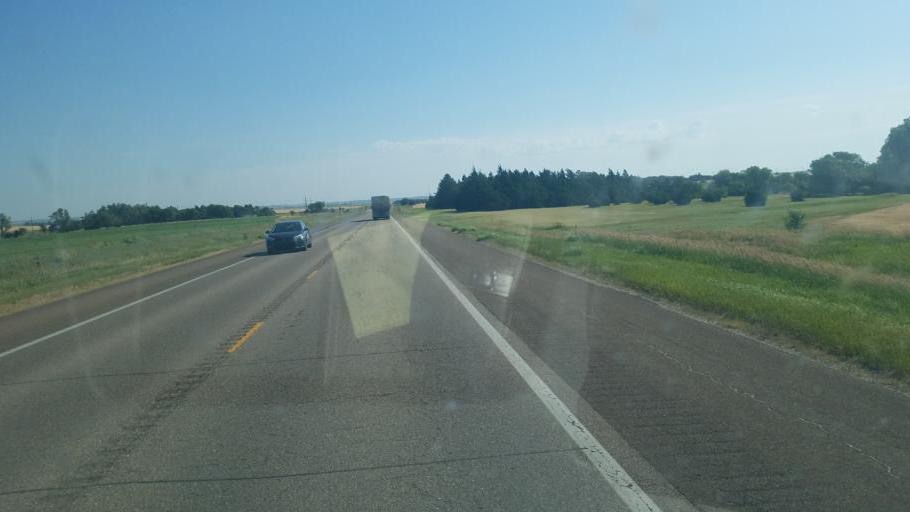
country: US
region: Kansas
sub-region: Barton County
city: Ellinwood
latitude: 38.4012
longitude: -98.6687
